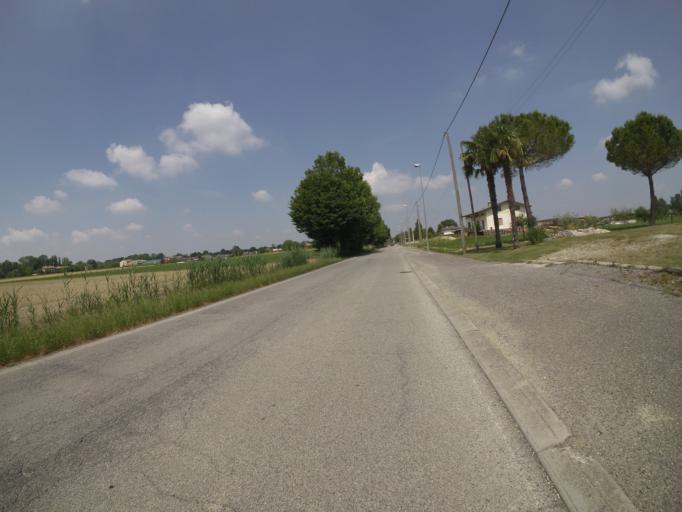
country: IT
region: Friuli Venezia Giulia
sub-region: Provincia di Udine
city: Teor
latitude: 45.8806
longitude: 13.0765
